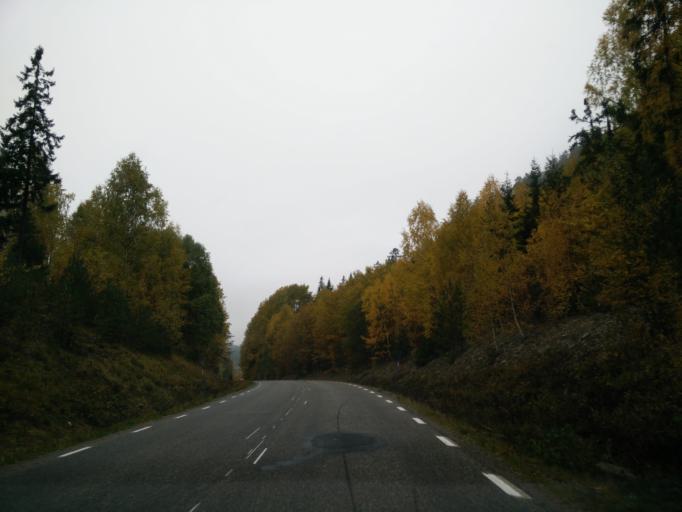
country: SE
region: Vaesternorrland
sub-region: Sundsvalls Kommun
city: Nolby
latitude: 62.3040
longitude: 17.2955
